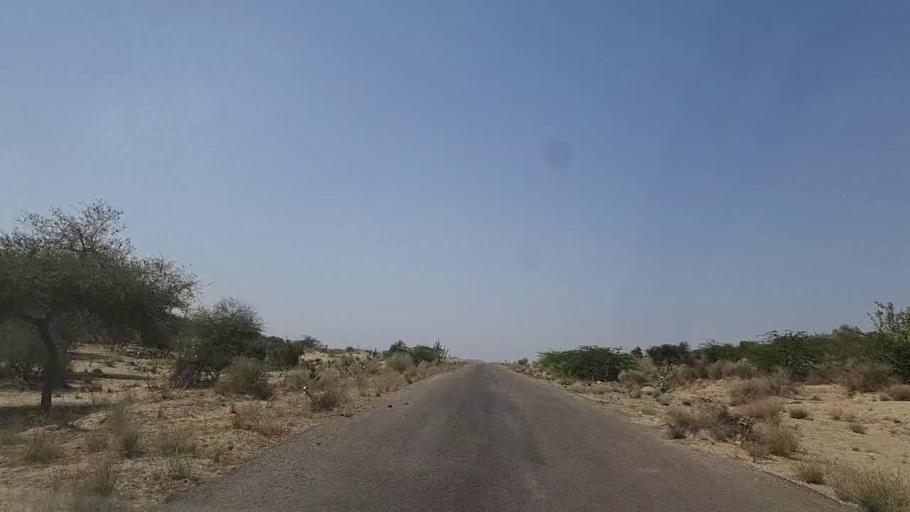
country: PK
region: Sindh
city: Diplo
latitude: 24.5693
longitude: 69.4721
